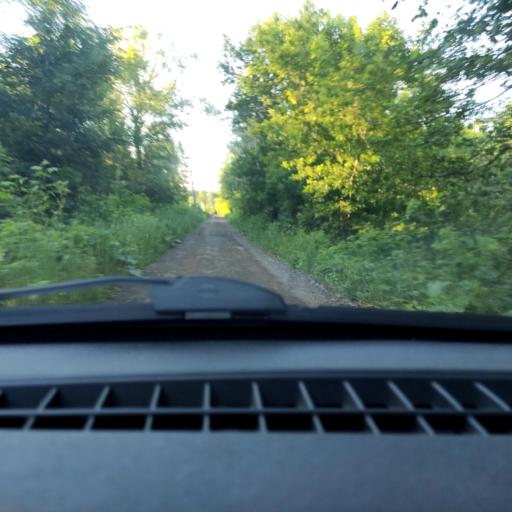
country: RU
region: Bashkortostan
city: Avdon
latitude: 54.6083
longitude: 55.6860
